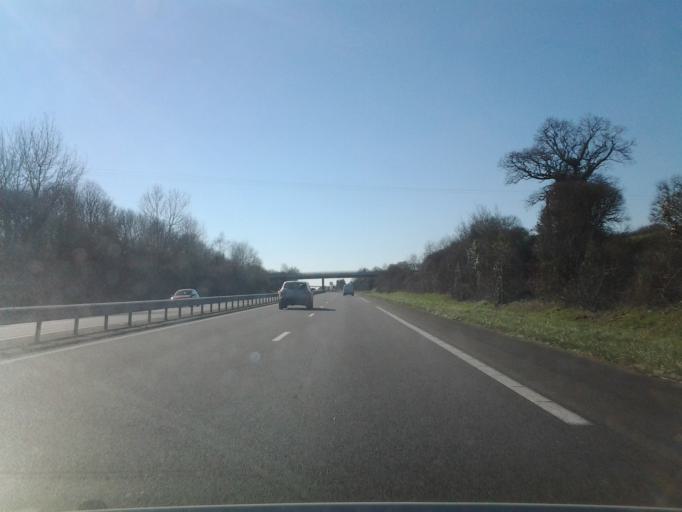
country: FR
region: Pays de la Loire
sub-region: Departement de la Vendee
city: Sainte-Flaive-des-Loups
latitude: 46.6287
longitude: -1.5789
